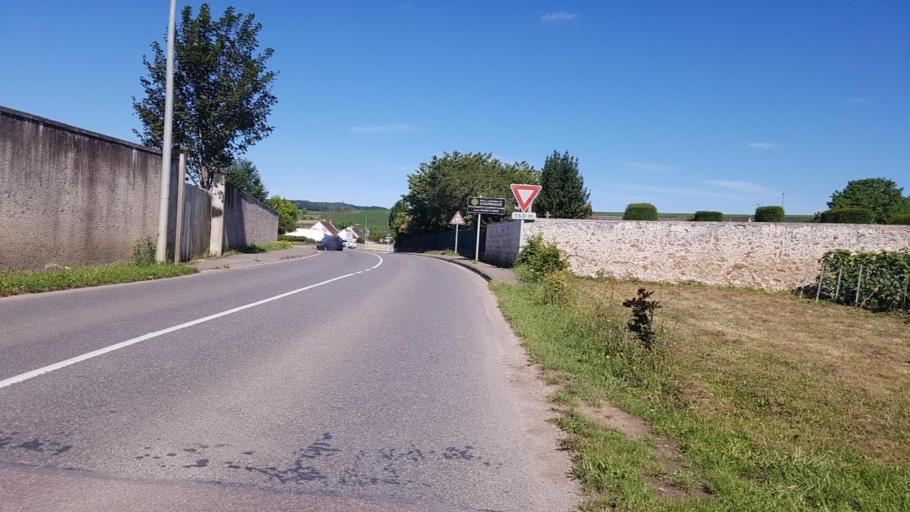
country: FR
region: Picardie
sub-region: Departement de l'Aisne
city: Charly-sur-Marne
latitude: 48.9794
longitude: 3.2885
